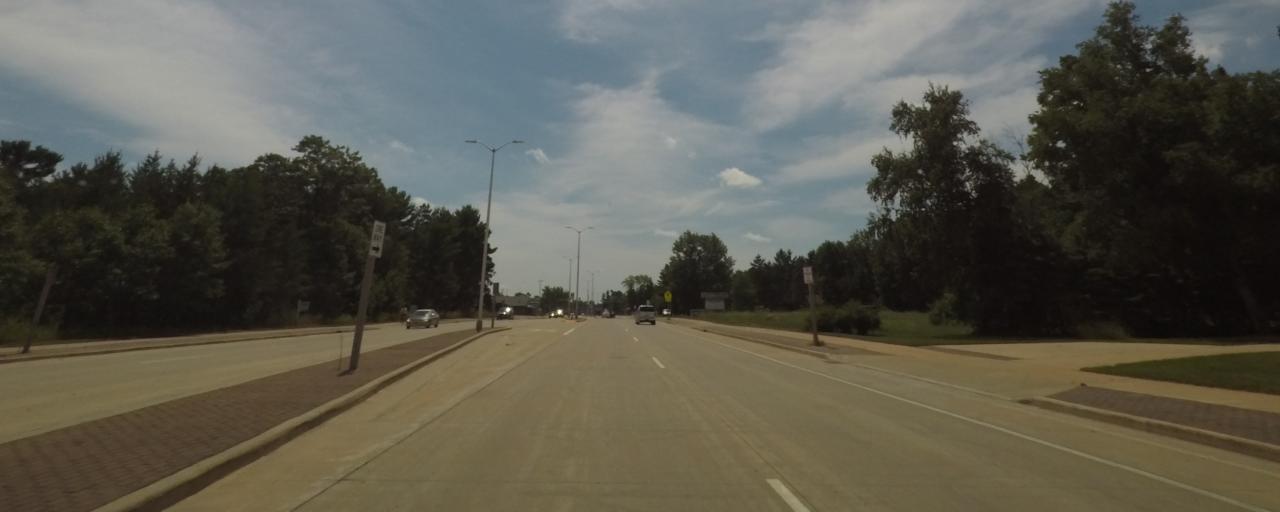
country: US
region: Wisconsin
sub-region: Portage County
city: Plover
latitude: 44.4671
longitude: -89.5459
